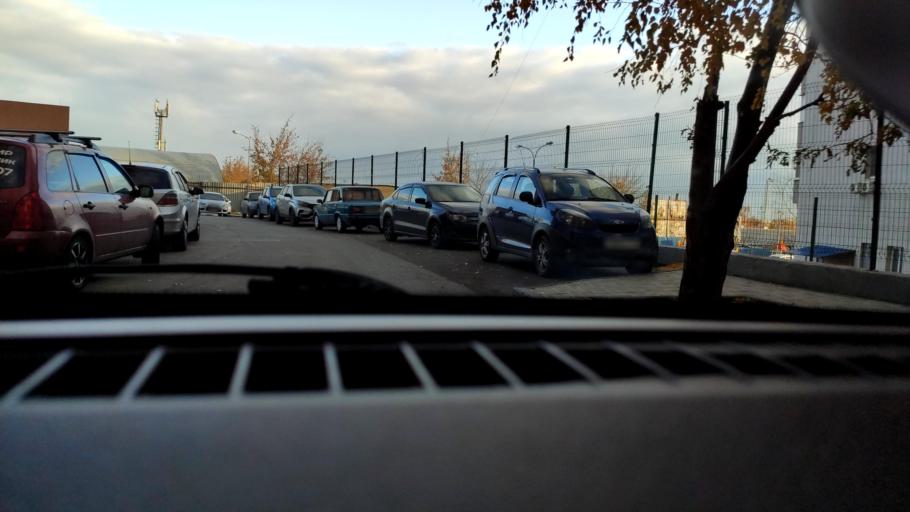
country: RU
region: Samara
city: Samara
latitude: 53.1866
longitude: 50.1354
